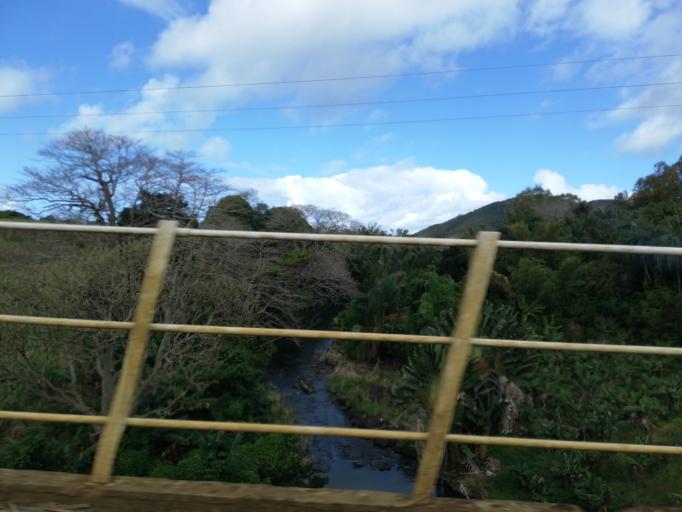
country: MU
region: Flacq
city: Grande Riviere Sud Est
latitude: -20.2777
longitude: 57.7596
